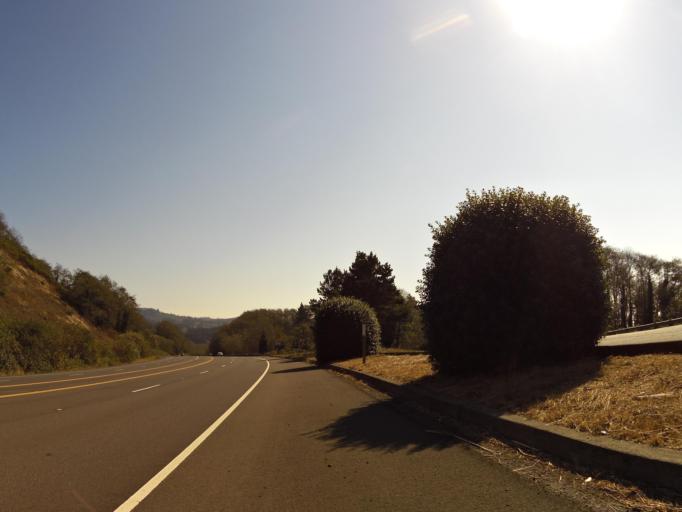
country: US
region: Oregon
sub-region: Tillamook County
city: Pacific City
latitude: 45.1420
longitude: -123.9694
